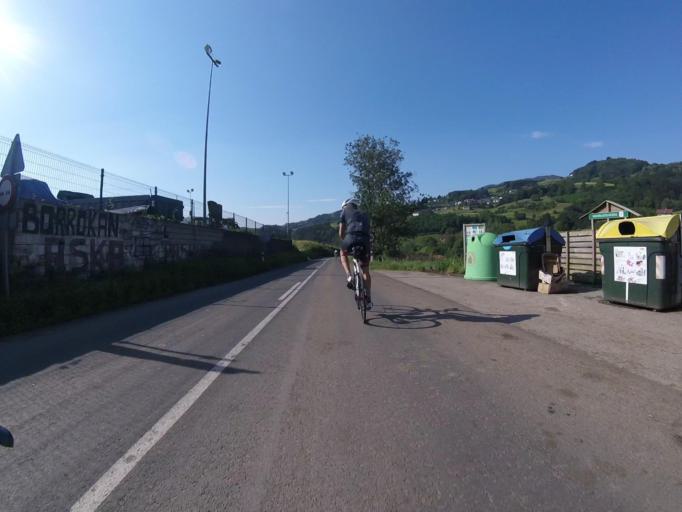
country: ES
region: Basque Country
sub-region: Provincia de Guipuzcoa
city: Asteasu
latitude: 43.1972
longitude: -2.0994
